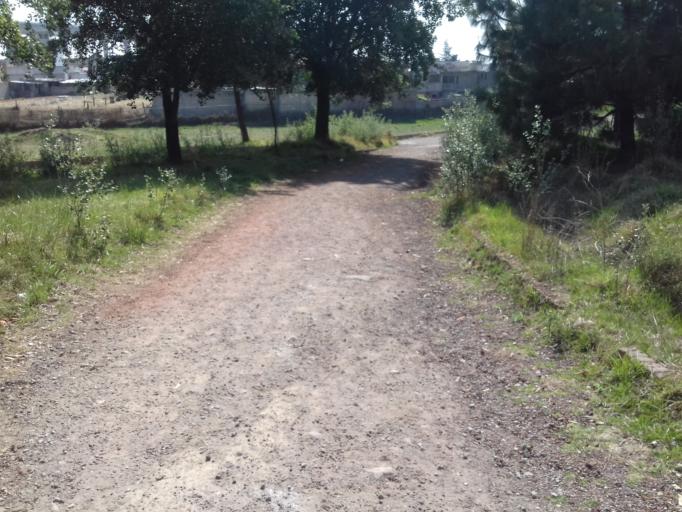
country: MX
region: Mexico
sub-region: Toluca
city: San Antonio Buenavista
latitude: 19.2788
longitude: -99.6957
